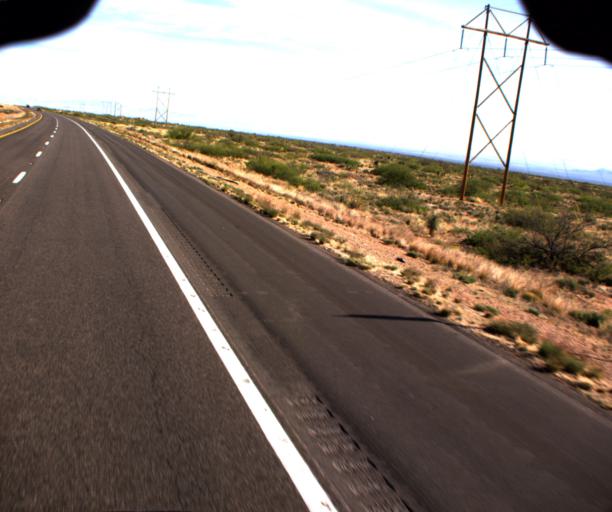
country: US
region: Arizona
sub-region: Graham County
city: Swift Trail Junction
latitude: 32.5234
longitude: -109.6734
